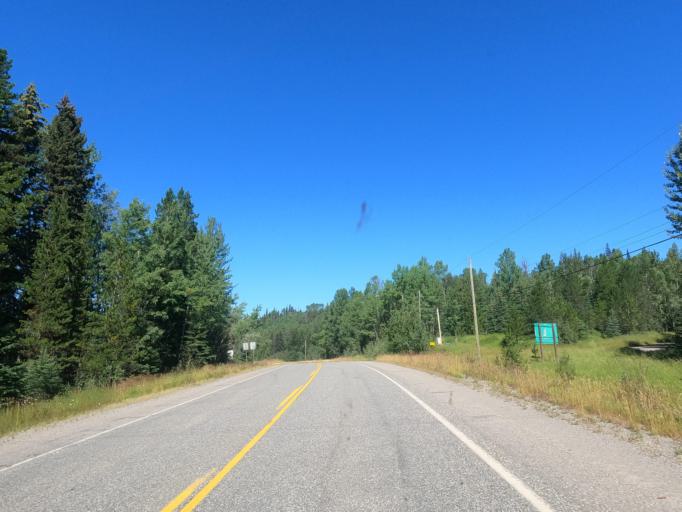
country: CA
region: British Columbia
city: Quesnel
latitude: 53.0518
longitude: -122.1548
